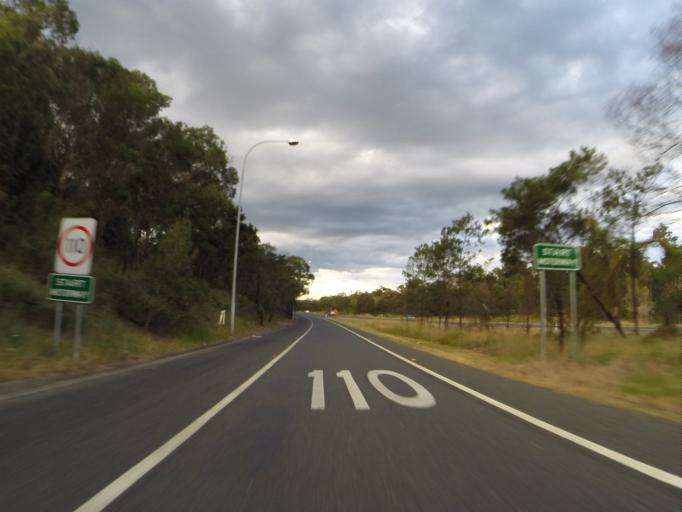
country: AU
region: New South Wales
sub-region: Wollondilly
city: Buxton
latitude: -34.3079
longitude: 150.6029
